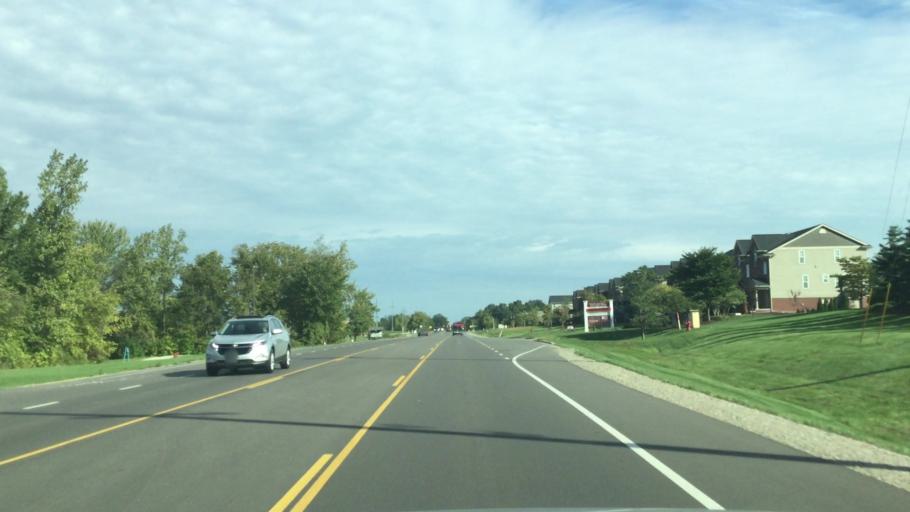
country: US
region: Michigan
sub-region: Livingston County
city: Howell
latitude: 42.6232
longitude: -83.8752
